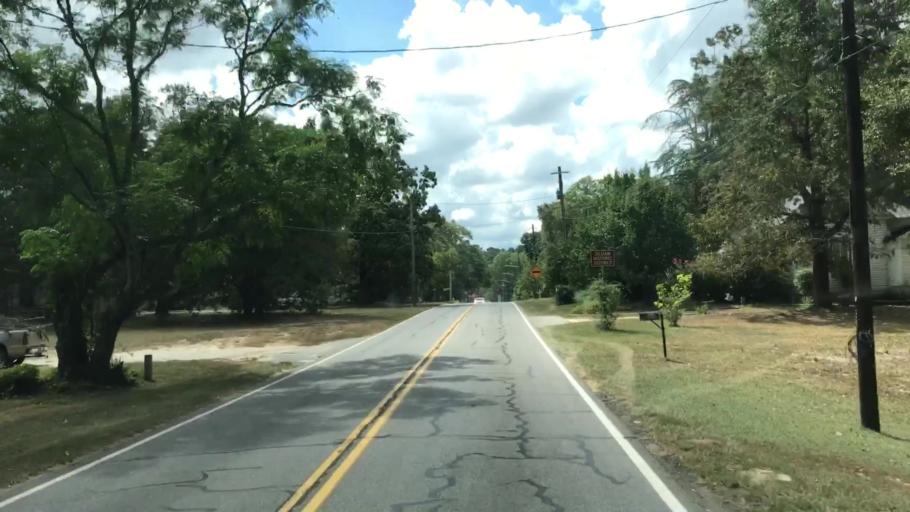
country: US
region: Georgia
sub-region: Greene County
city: Union Point
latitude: 33.5394
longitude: -83.0806
